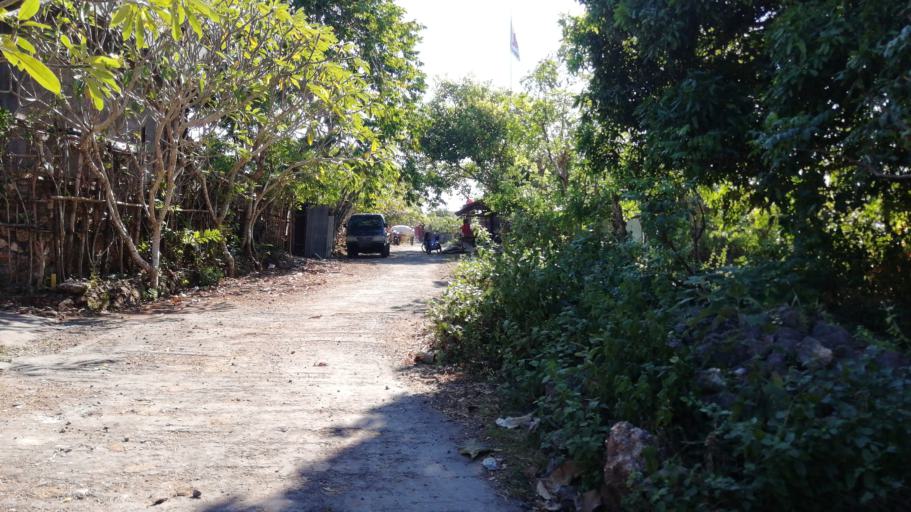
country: ID
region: Bali
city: Jimbaran
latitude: -8.8089
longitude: 115.1618
